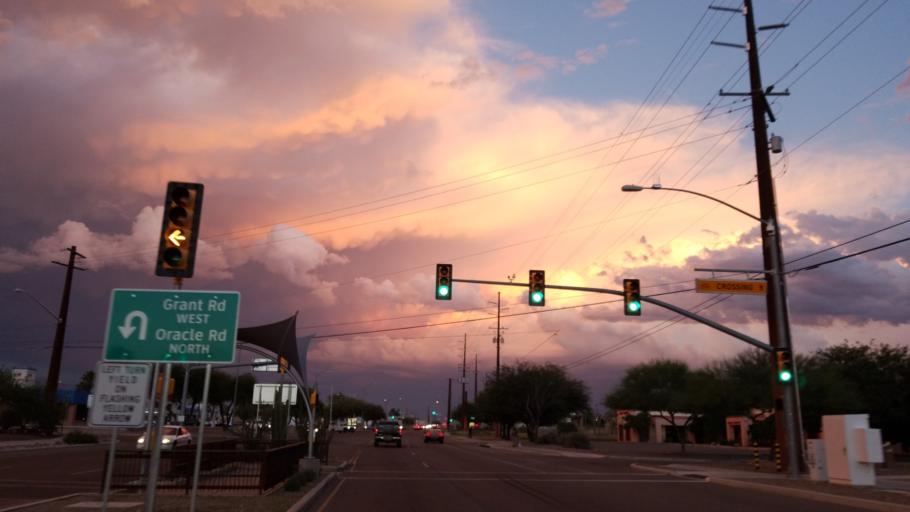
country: US
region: Arizona
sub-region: Pima County
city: South Tucson
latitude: 32.2502
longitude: -110.9748
